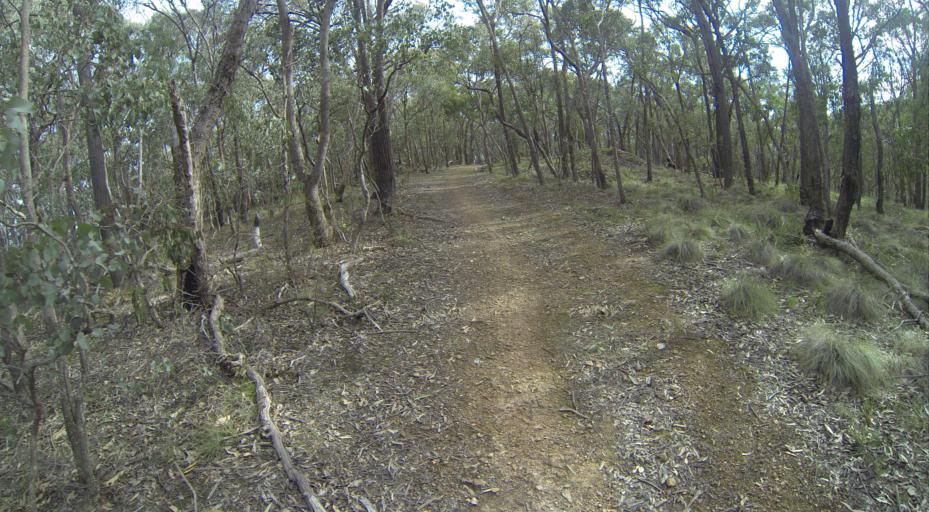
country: AU
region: Victoria
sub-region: Nillumbik
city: Saint Andrews
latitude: -37.6318
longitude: 145.3021
